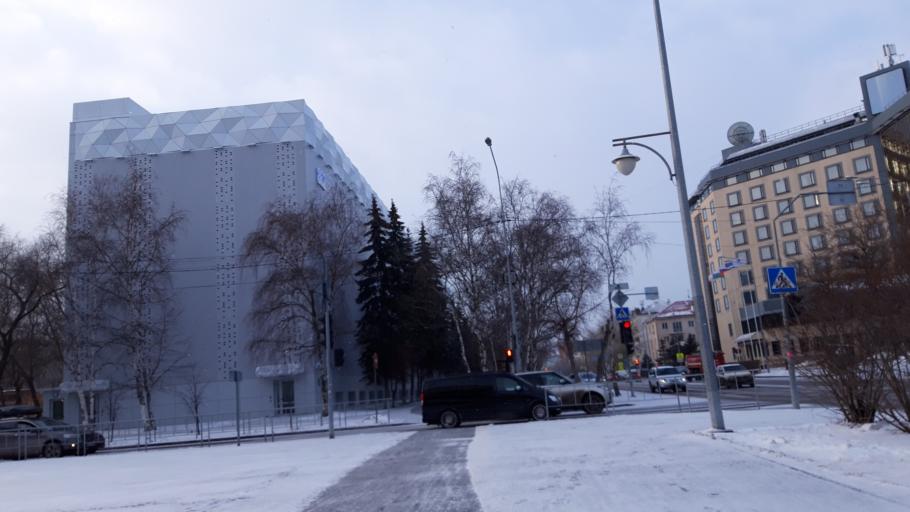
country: RU
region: Tjumen
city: Tyumen
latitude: 57.1538
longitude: 65.5492
